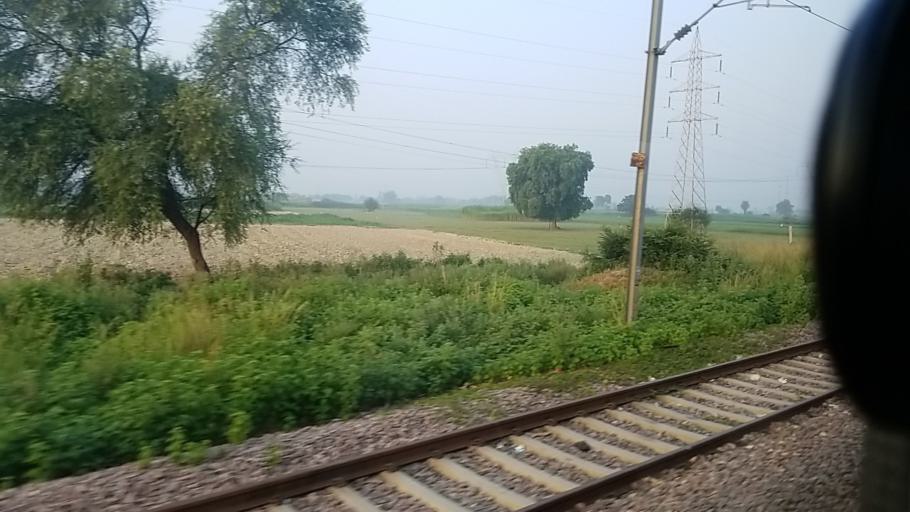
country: IN
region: Uttar Pradesh
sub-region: Kanpur
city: Nawabganj
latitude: 26.4650
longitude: 80.1700
